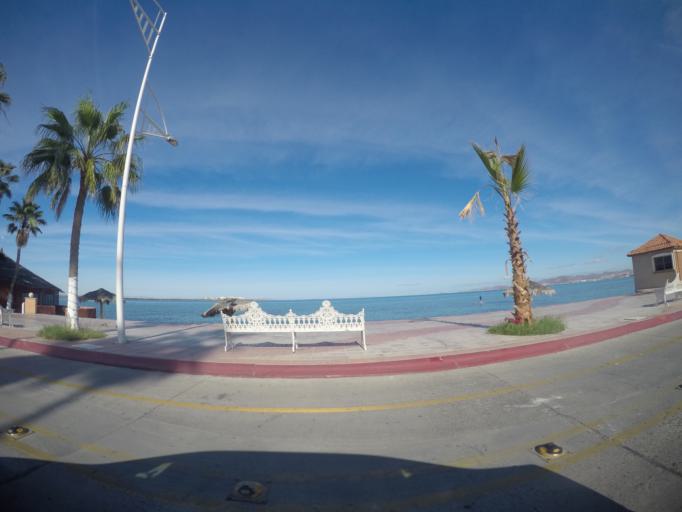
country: MX
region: Baja California Sur
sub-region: La Paz
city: La Paz
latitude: 24.1927
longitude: -110.2955
